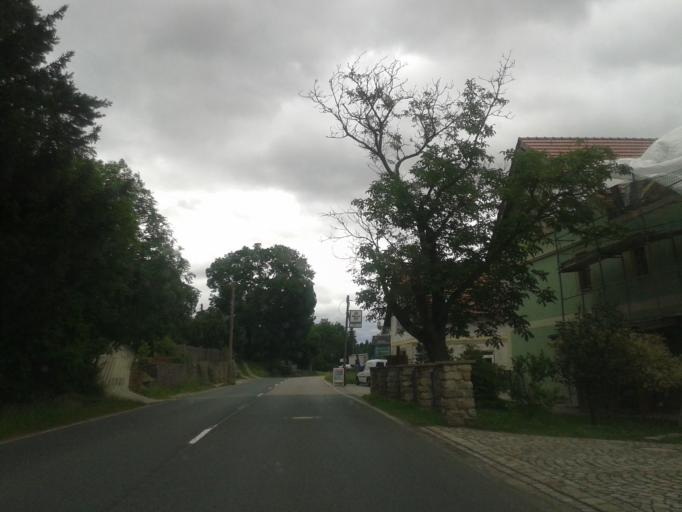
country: DE
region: Saxony
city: Wilsdruff
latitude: 51.0220
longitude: 13.5568
